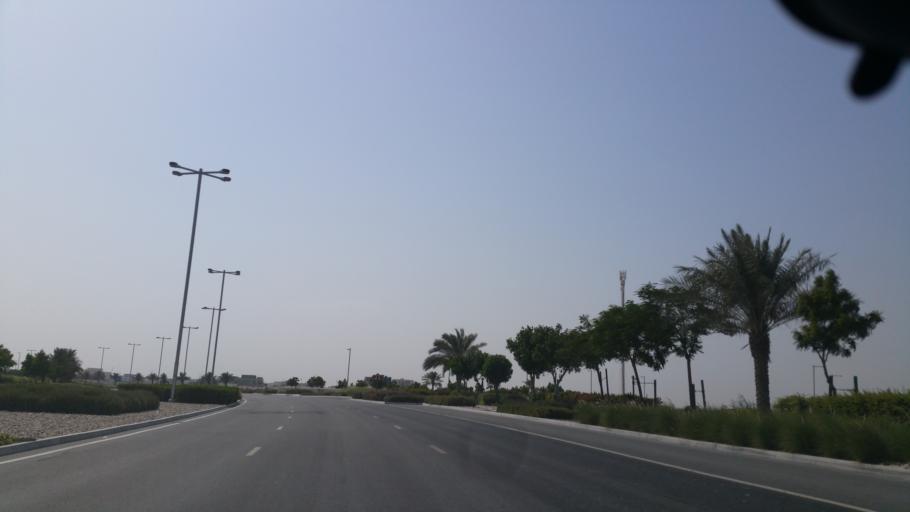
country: QA
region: Baladiyat Umm Salal
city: Umm Salal Muhammad
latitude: 25.4401
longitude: 51.5126
